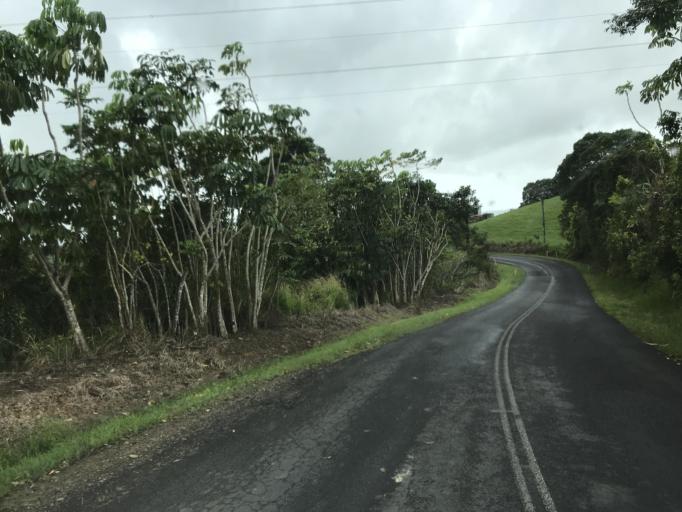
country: AU
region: Queensland
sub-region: Cassowary Coast
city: Innisfail
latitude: -17.5172
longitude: 145.9716
